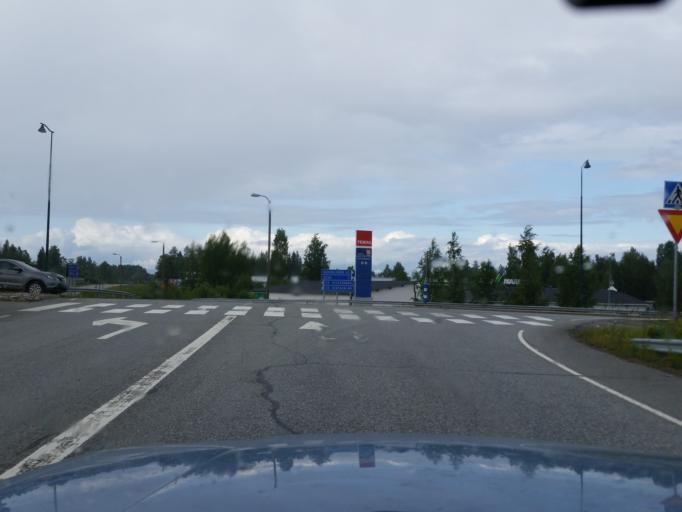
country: FI
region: Southern Savonia
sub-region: Pieksaemaeki
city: Juva
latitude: 61.8984
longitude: 27.8042
